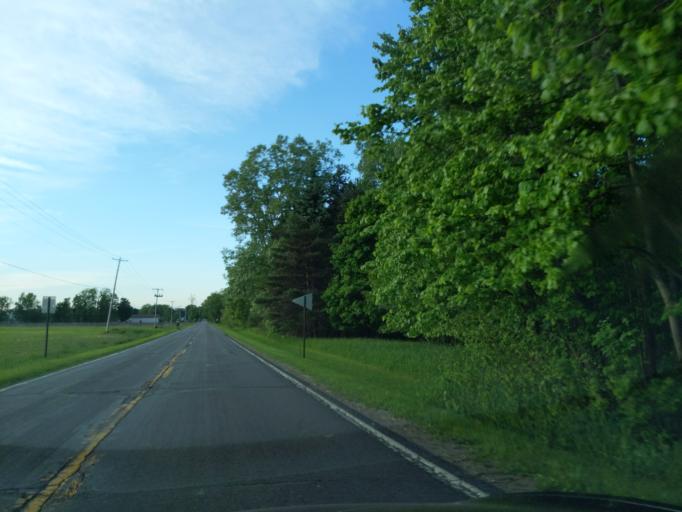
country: US
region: Michigan
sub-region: Ingham County
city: Mason
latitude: 42.5451
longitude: -84.3028
